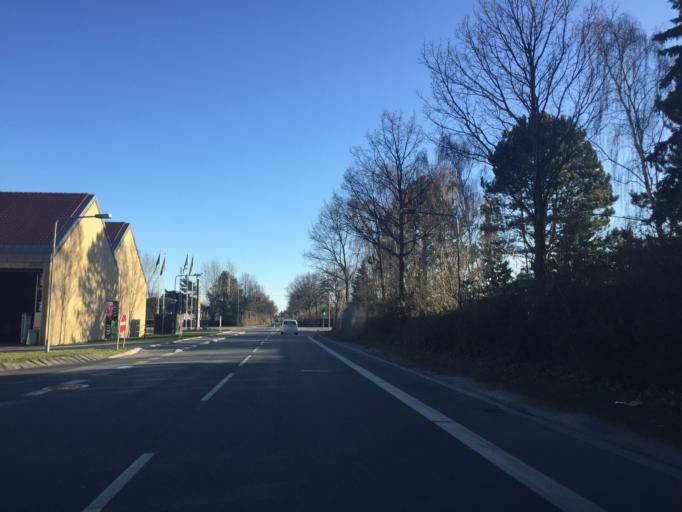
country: DK
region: Capital Region
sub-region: Dragor Kommune
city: Dragor
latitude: 55.5960
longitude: 12.6581
